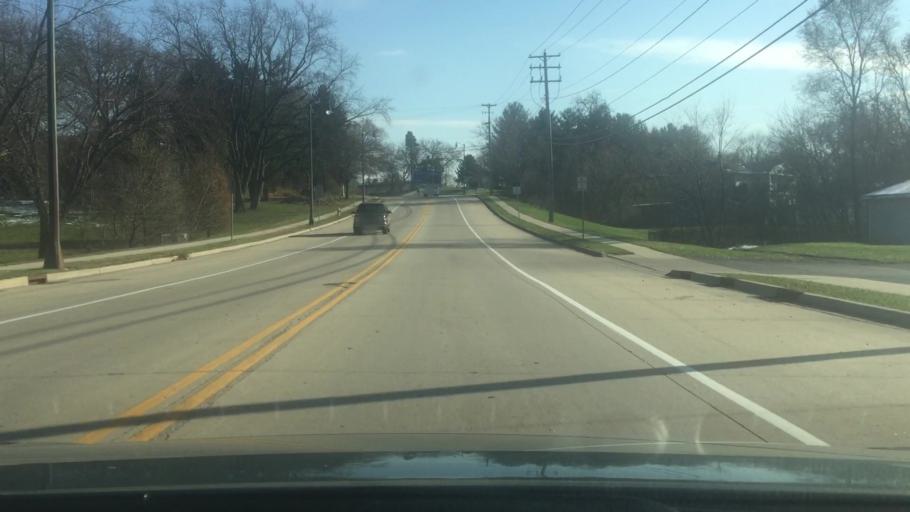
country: US
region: Wisconsin
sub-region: Jefferson County
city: Fort Atkinson
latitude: 42.9370
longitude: -88.8538
